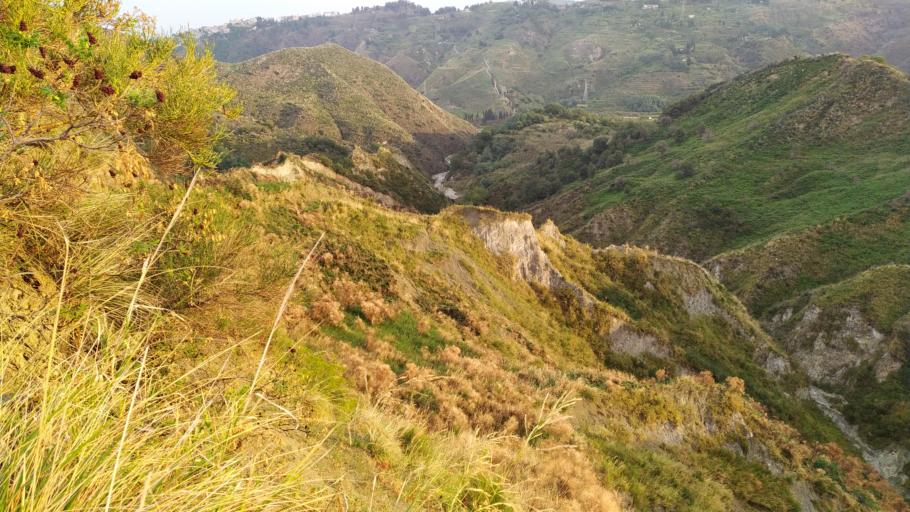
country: IT
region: Sicily
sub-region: Messina
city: Villafranca Tirrena
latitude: 38.2163
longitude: 15.4730
